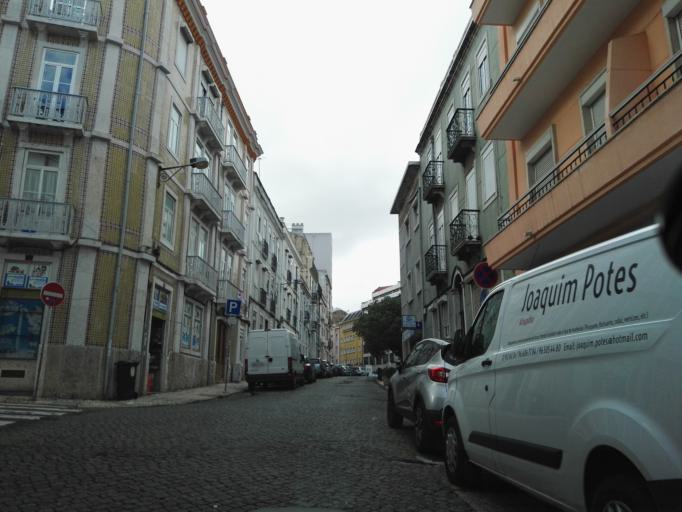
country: PT
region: Lisbon
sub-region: Lisbon
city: Lisbon
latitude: 38.7339
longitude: -9.1384
